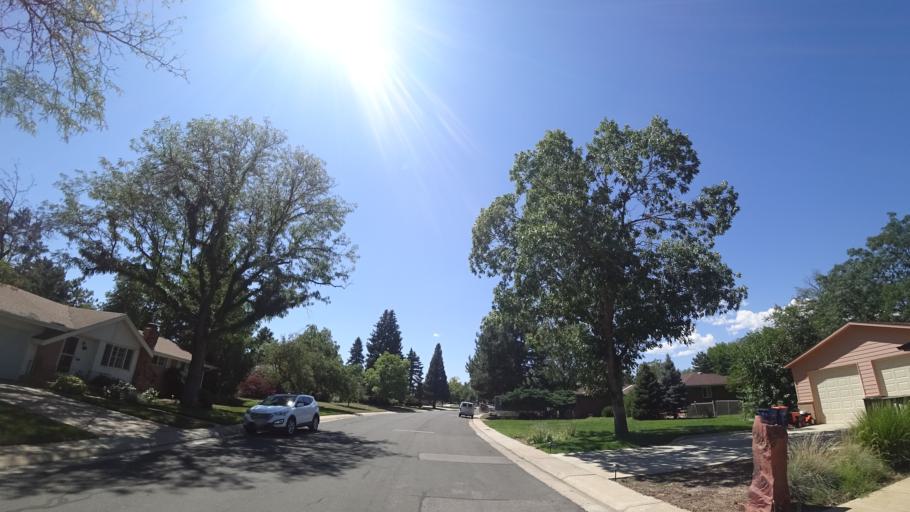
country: US
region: Colorado
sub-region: Arapahoe County
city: Greenwood Village
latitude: 39.6084
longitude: -104.9551
